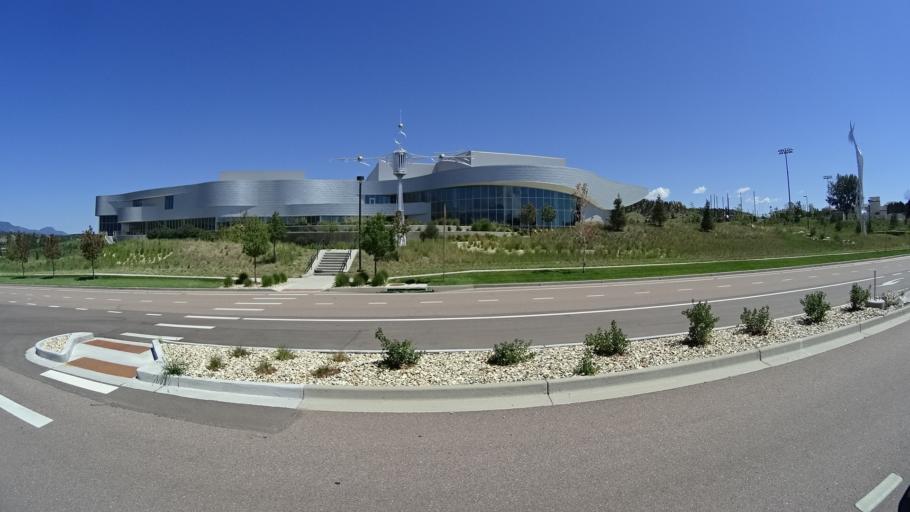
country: US
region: Colorado
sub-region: El Paso County
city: Colorado Springs
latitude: 38.9035
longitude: -104.8155
